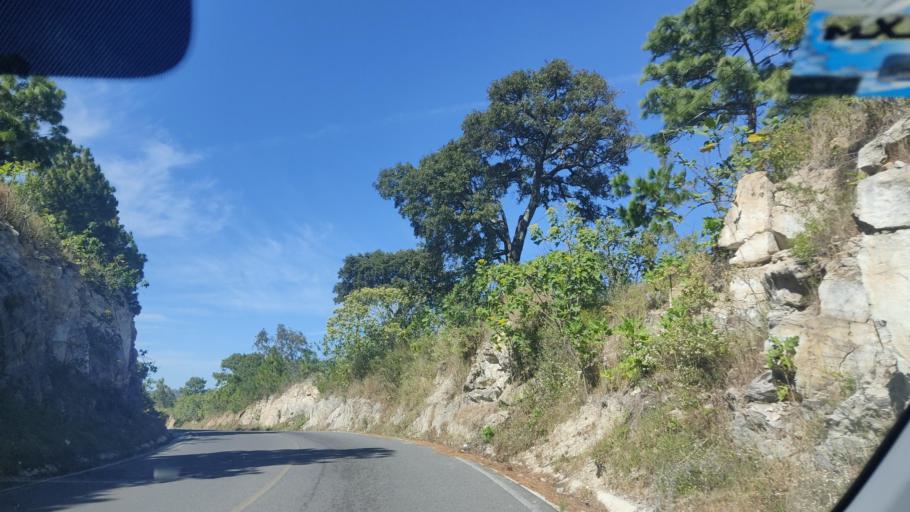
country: MX
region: Nayarit
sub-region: Jala
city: Rosa Blanca
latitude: 21.1012
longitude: -104.3640
